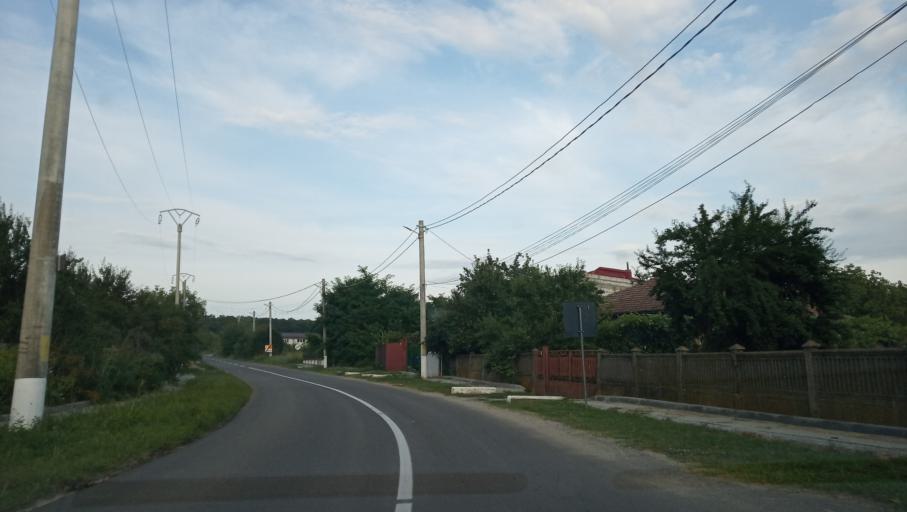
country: RO
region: Giurgiu
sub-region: Comuna Comana
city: Comana
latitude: 44.1690
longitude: 26.1547
